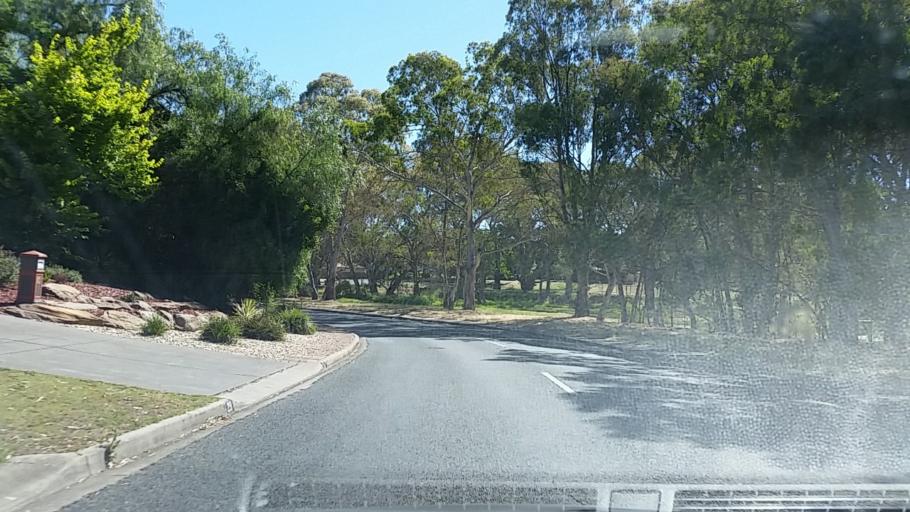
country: AU
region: South Australia
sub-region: Tea Tree Gully
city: Hope Valley
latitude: -34.8035
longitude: 138.6961
